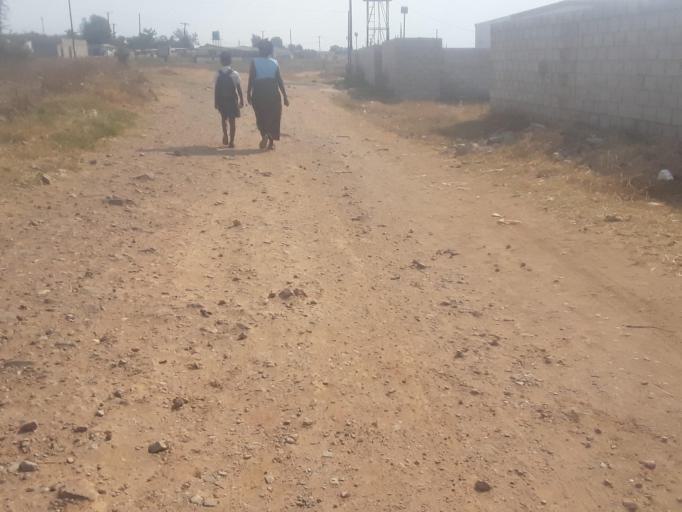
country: ZM
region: Lusaka
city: Lusaka
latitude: -15.3692
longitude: 28.2968
